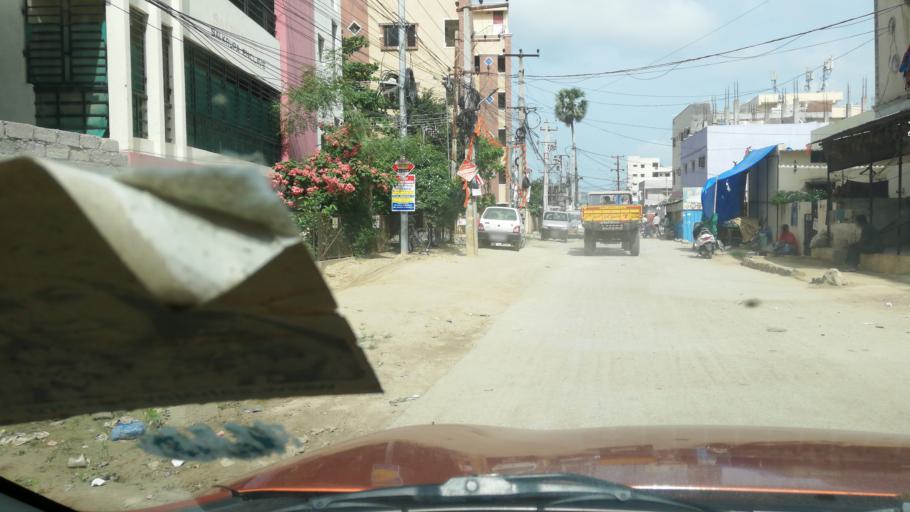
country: IN
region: Telangana
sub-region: Rangareddi
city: Kukatpalli
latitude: 17.4144
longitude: 78.3669
